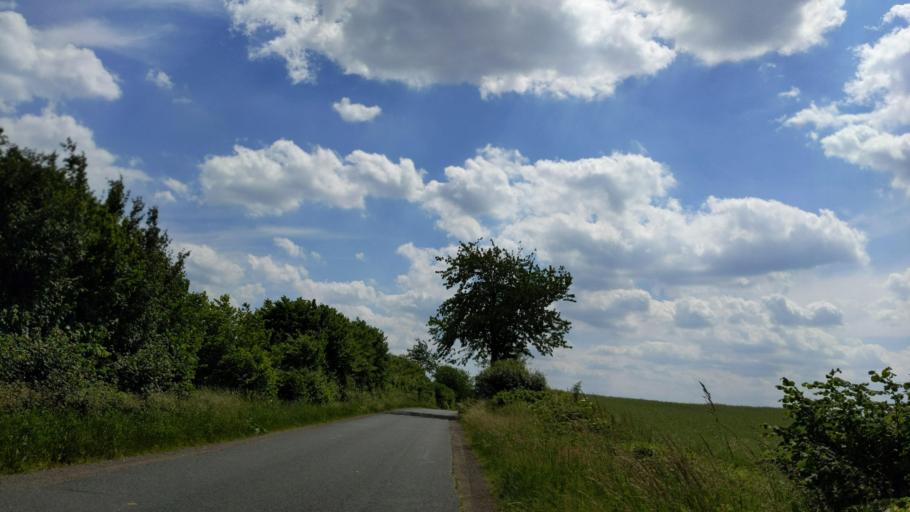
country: DE
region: Schleswig-Holstein
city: Bak
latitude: 53.7179
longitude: 10.7753
